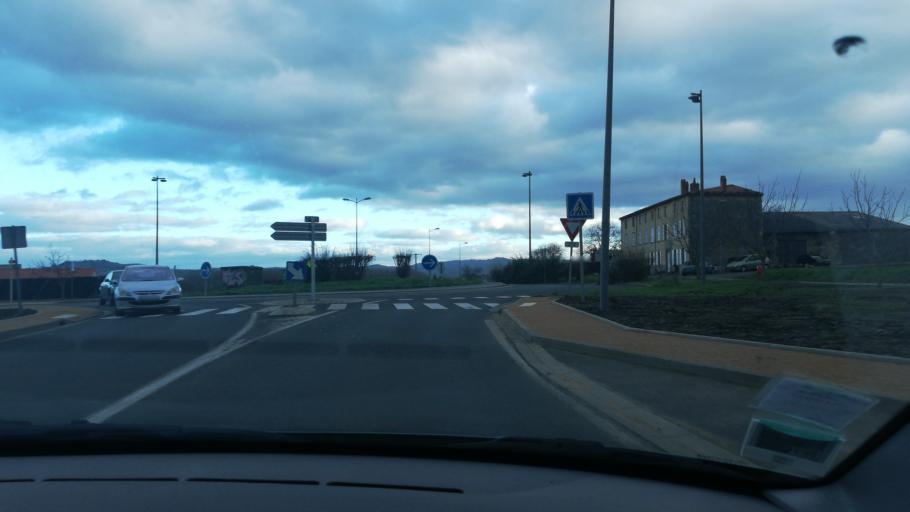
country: FR
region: Auvergne
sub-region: Departement du Puy-de-Dome
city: Vertaizon
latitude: 45.7630
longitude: 3.3069
